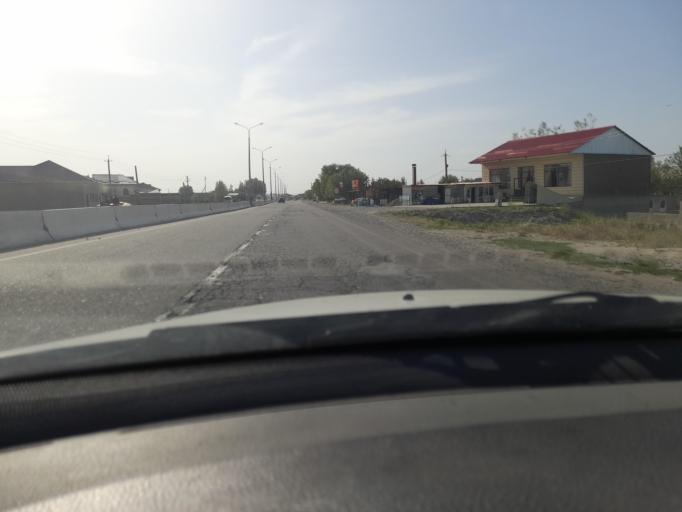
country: UZ
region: Samarqand
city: Kattaqo'rg'on
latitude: 39.9214
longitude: 66.2905
